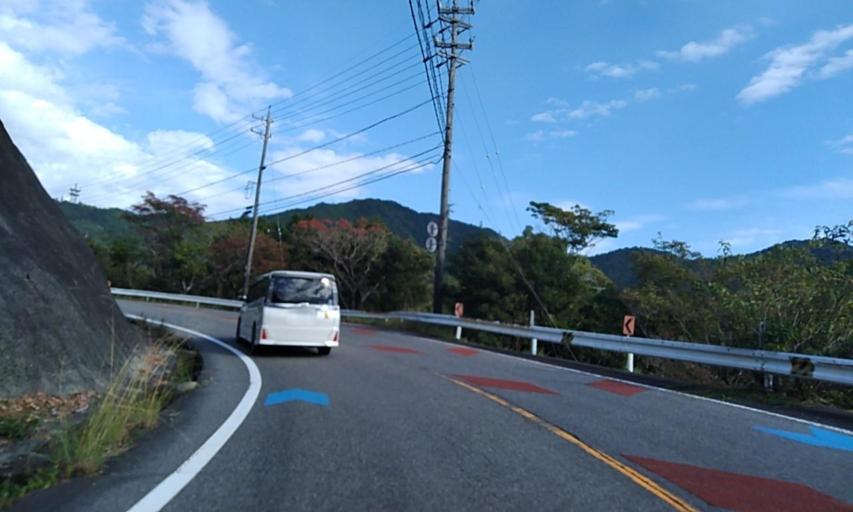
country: JP
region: Mie
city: Owase
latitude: 34.2108
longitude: 136.3616
